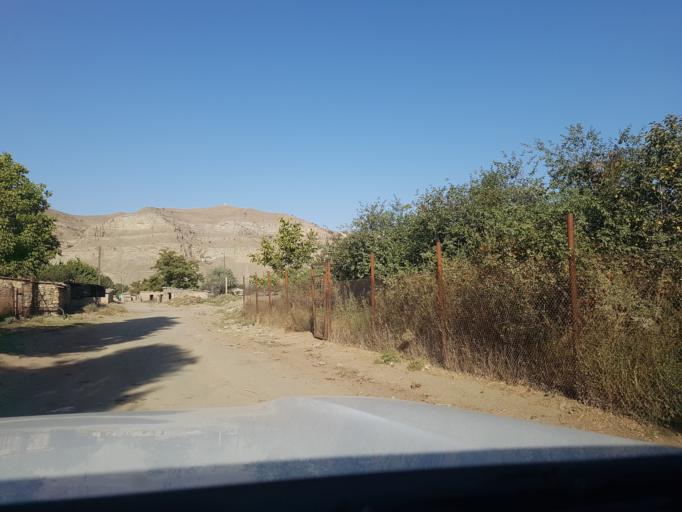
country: TM
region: Balkan
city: Magtymguly
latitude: 38.3008
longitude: 56.7481
